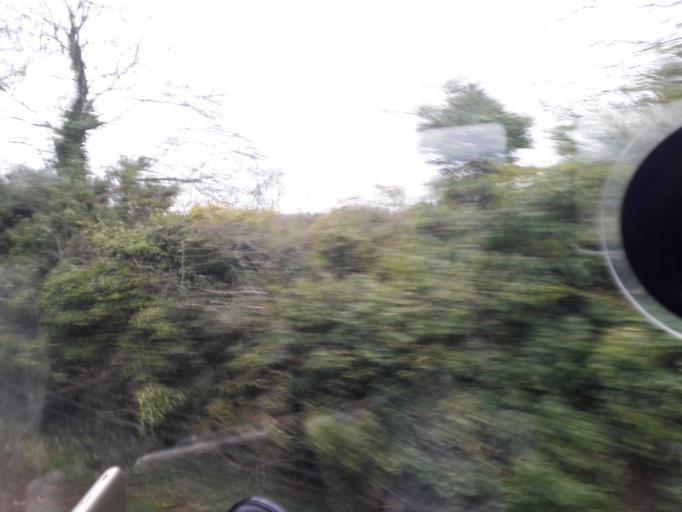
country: IE
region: Leinster
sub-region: An Longfort
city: Edgeworthstown
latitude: 53.6922
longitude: -7.6221
